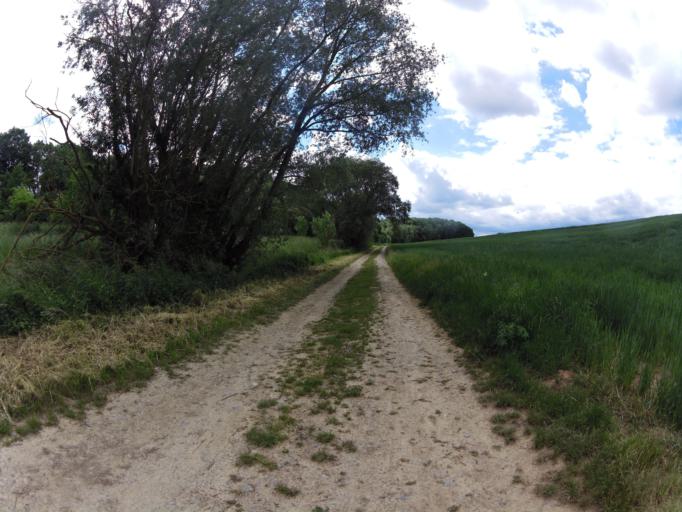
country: DE
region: Bavaria
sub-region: Regierungsbezirk Unterfranken
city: Gaukonigshofen
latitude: 49.6712
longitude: 9.9990
